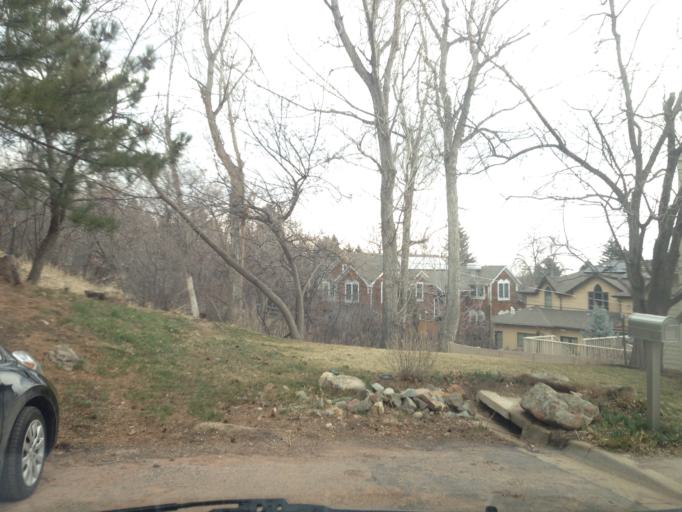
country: US
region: Colorado
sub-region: Boulder County
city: Boulder
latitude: 40.0335
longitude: -105.2925
